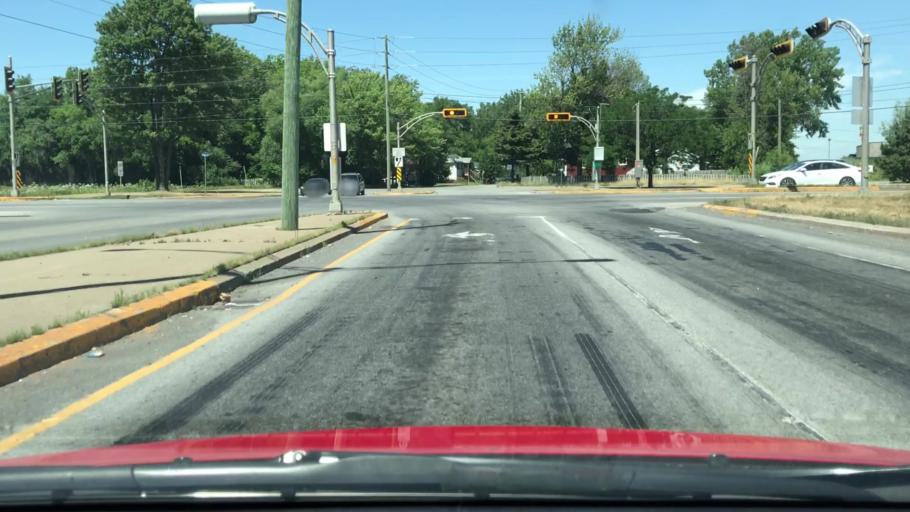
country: CA
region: Quebec
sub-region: Monteregie
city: Saint-Constant
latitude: 45.3950
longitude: -73.6033
